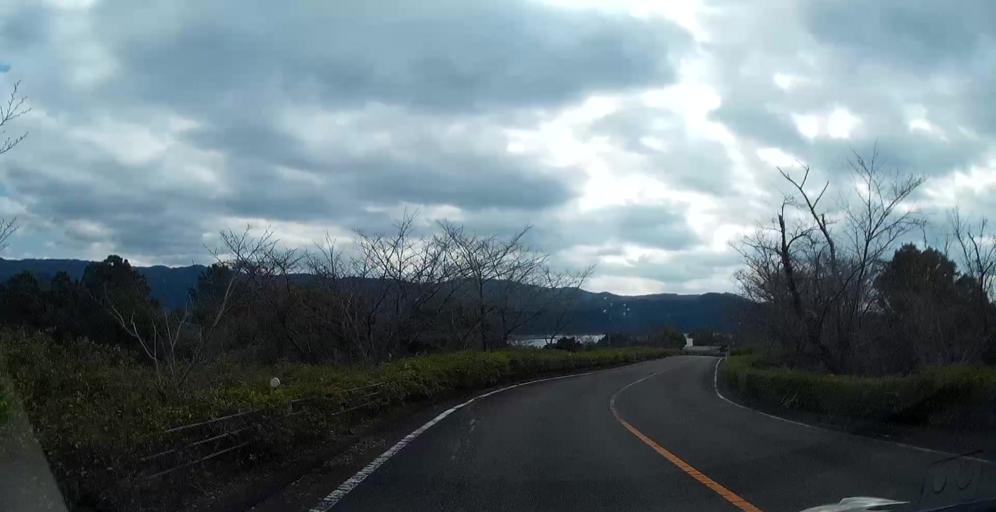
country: JP
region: Kumamoto
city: Minamata
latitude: 32.3647
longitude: 130.4910
